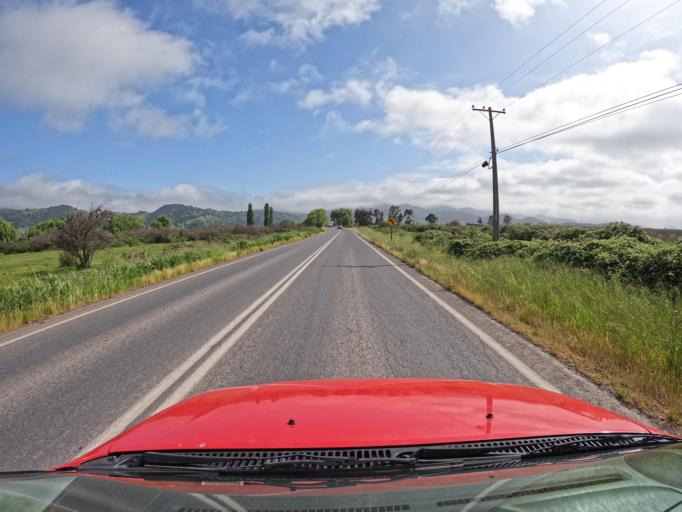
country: CL
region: Maule
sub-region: Provincia de Curico
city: Teno
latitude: -34.8428
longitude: -71.1866
